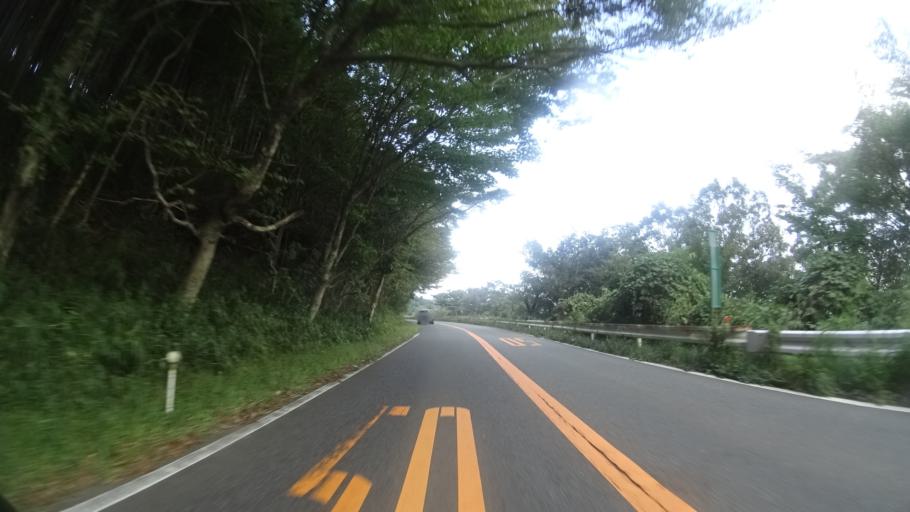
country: JP
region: Oita
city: Beppu
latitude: 33.2685
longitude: 131.4192
